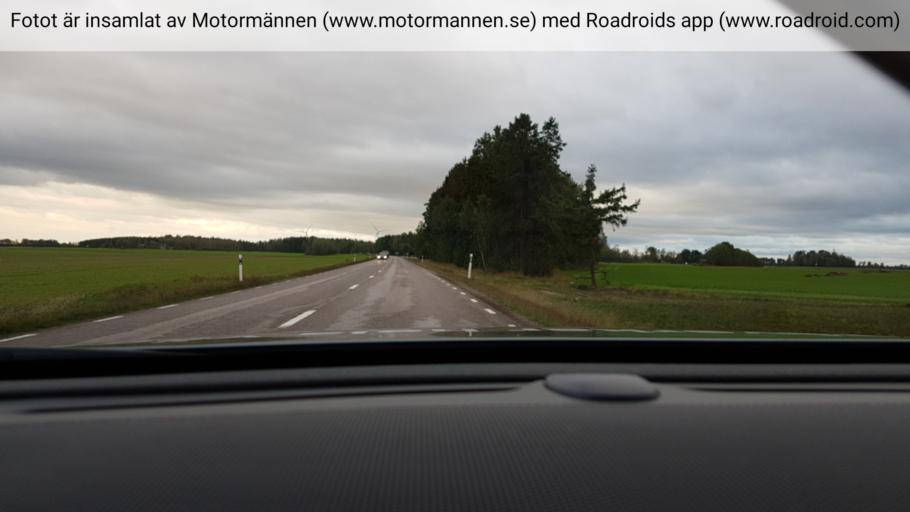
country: SE
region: Vaestra Goetaland
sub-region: Vanersborgs Kommun
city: Bralanda
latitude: 58.6134
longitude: 12.4152
